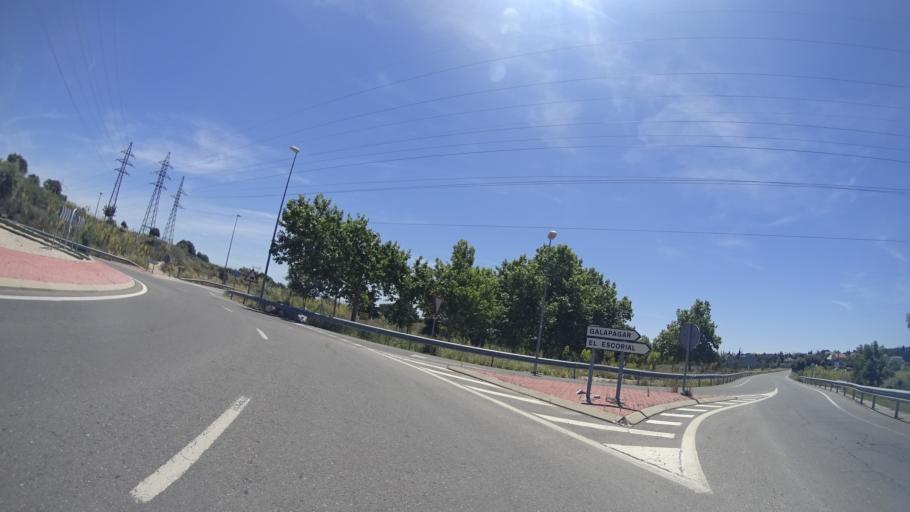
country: ES
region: Madrid
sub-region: Provincia de Madrid
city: Galapagar
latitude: 40.5918
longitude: -4.0115
